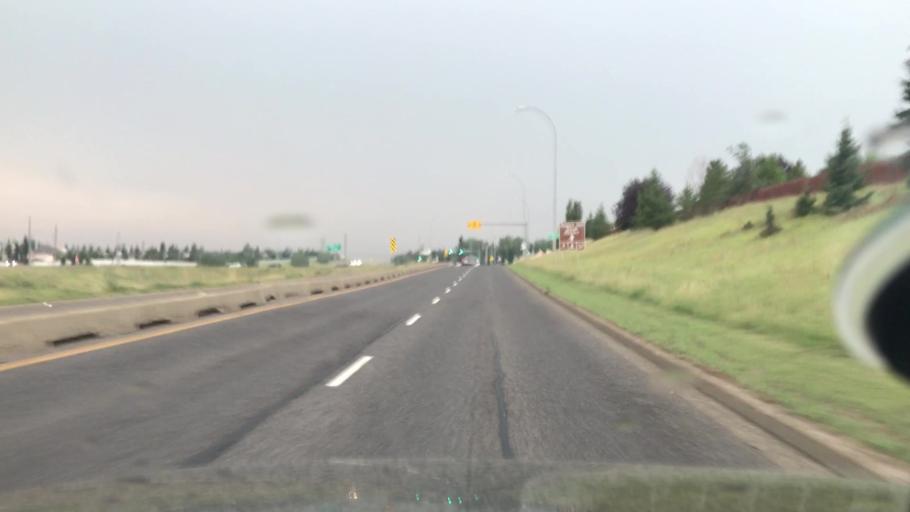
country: CA
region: Alberta
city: Edmonton
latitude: 53.4708
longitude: -113.5803
